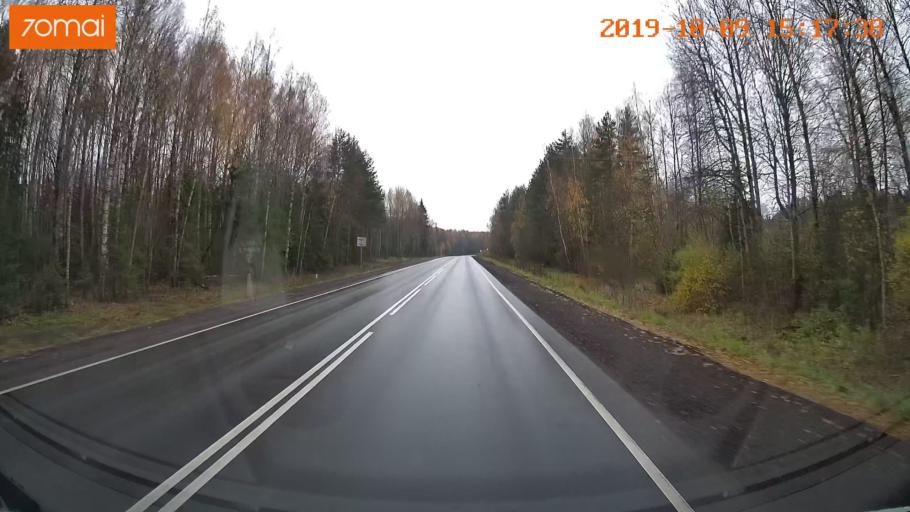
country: RU
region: Kostroma
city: Susanino
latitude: 58.0957
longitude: 41.5820
